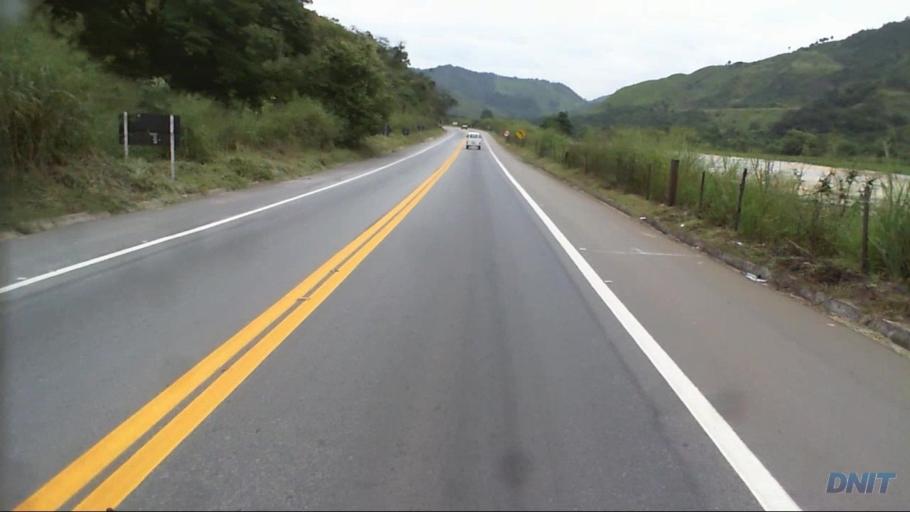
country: BR
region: Minas Gerais
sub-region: Timoteo
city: Timoteo
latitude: -19.6080
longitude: -42.7634
